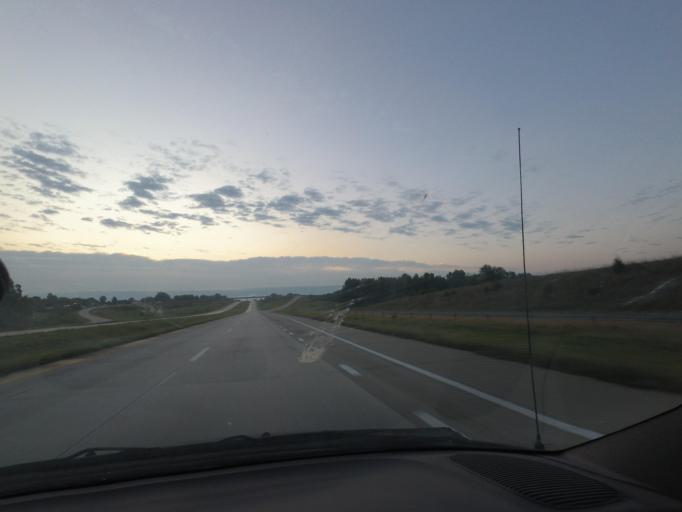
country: US
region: Missouri
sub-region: Macon County
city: Macon
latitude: 39.7565
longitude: -92.6330
